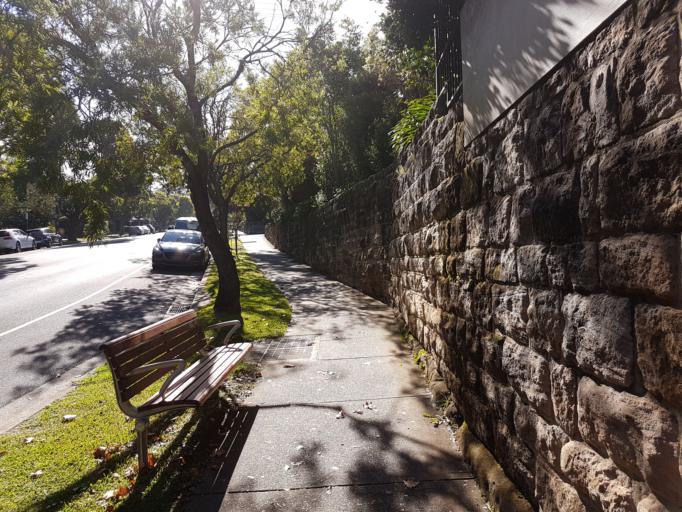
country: AU
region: New South Wales
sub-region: North Sydney
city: North Sydney
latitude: -33.8371
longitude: 151.1999
